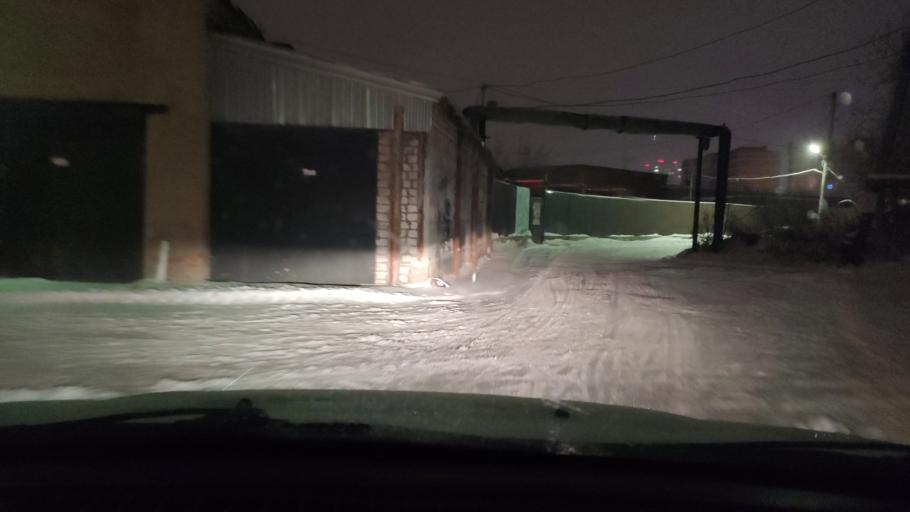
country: RU
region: Perm
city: Kondratovo
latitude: 57.9827
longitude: 56.1088
